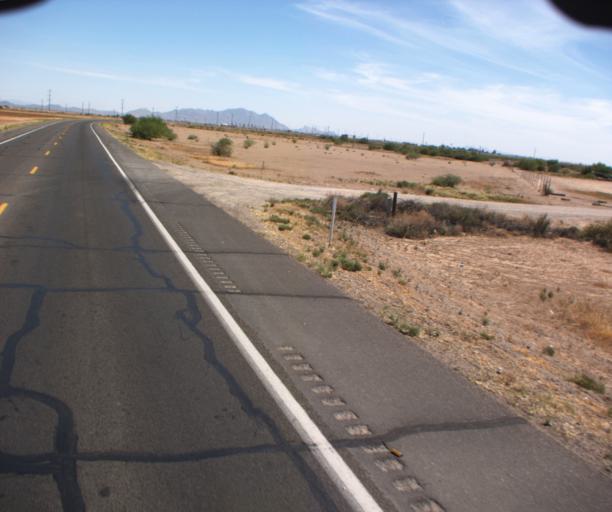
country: US
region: Arizona
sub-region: Pinal County
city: Coolidge
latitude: 32.9499
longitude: -111.5198
